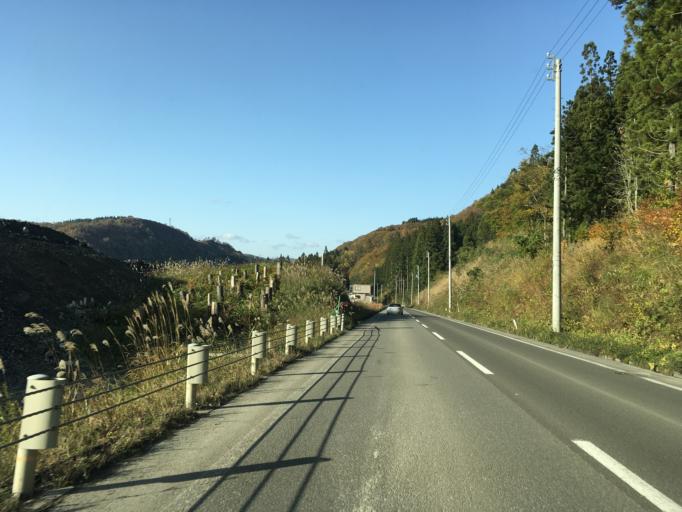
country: JP
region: Akita
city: Yuzawa
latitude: 39.0564
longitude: 140.7238
